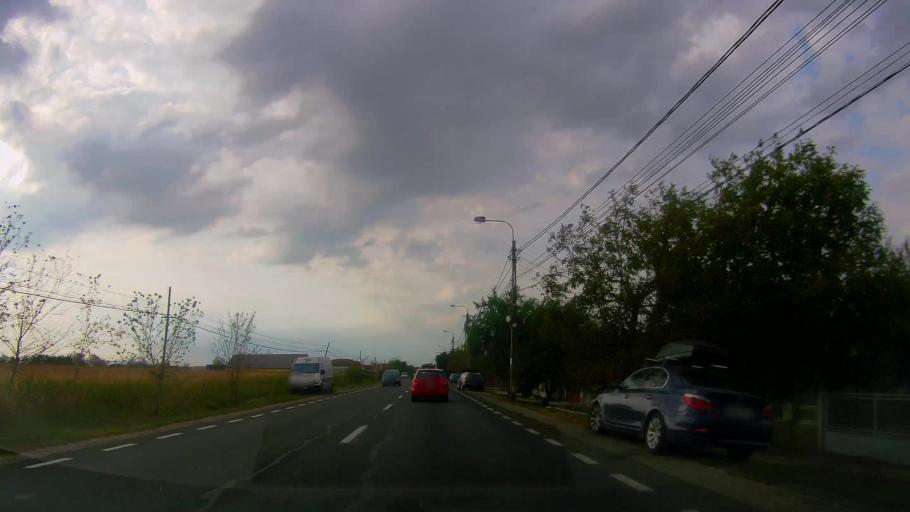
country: RO
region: Satu Mare
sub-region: Comuna Paulesti
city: Paulesti
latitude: 47.7478
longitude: 22.8829
